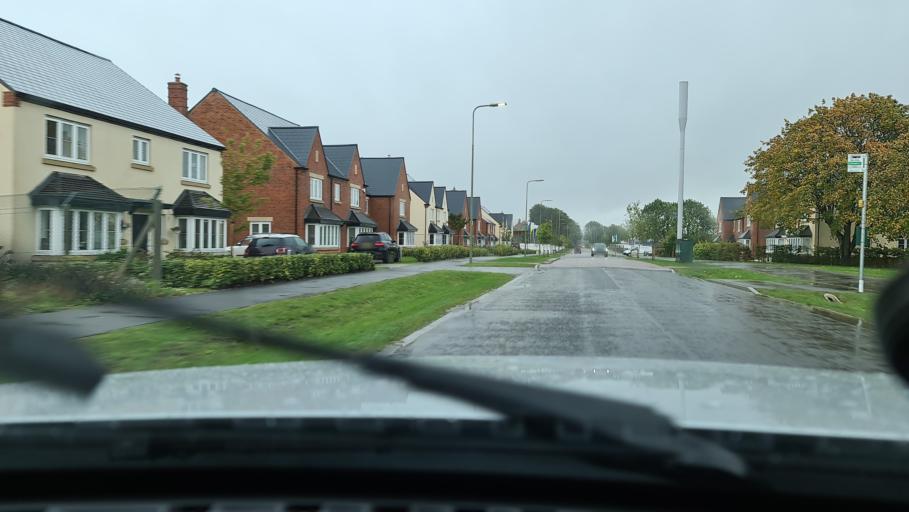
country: GB
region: England
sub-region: Oxfordshire
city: Somerton
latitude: 51.9289
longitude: -1.2628
